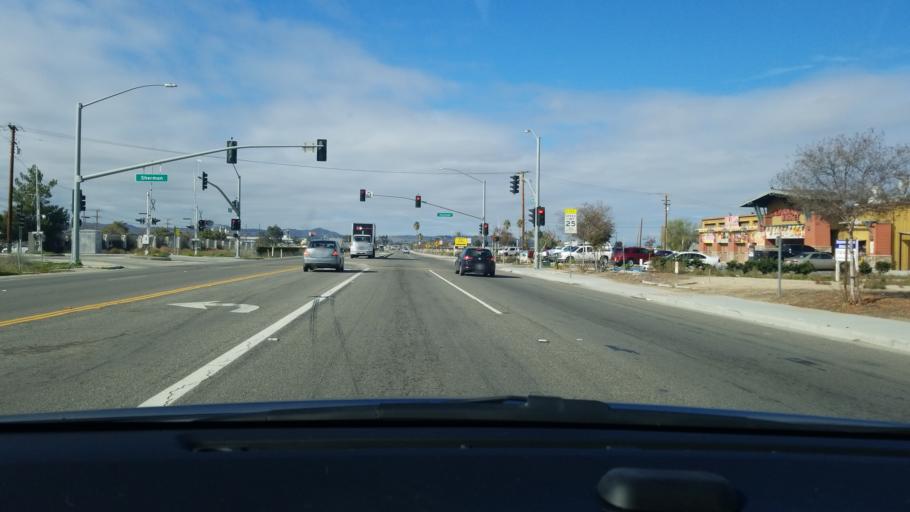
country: US
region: California
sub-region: Riverside County
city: Romoland
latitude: 33.7484
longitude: -117.1795
